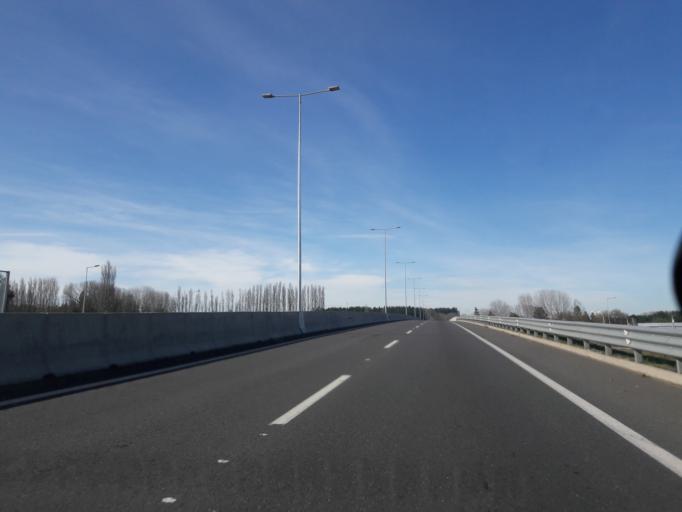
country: CL
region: Biobio
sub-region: Provincia de Biobio
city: Cabrero
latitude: -37.0302
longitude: -72.4313
